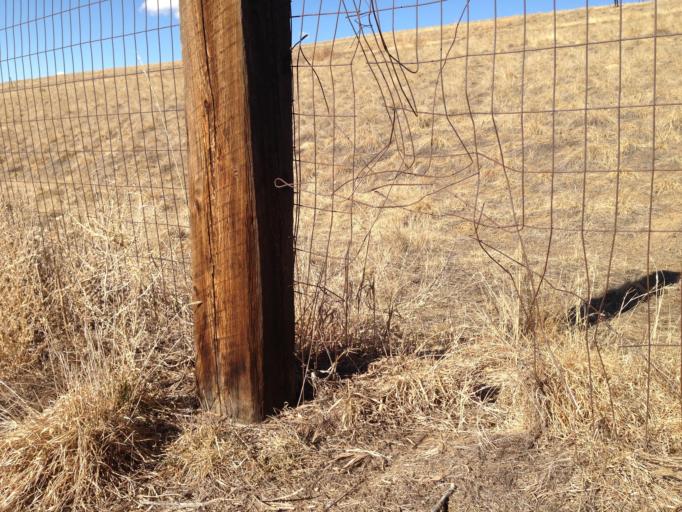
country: US
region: Colorado
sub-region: Boulder County
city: Erie
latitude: 40.0294
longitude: -105.0340
